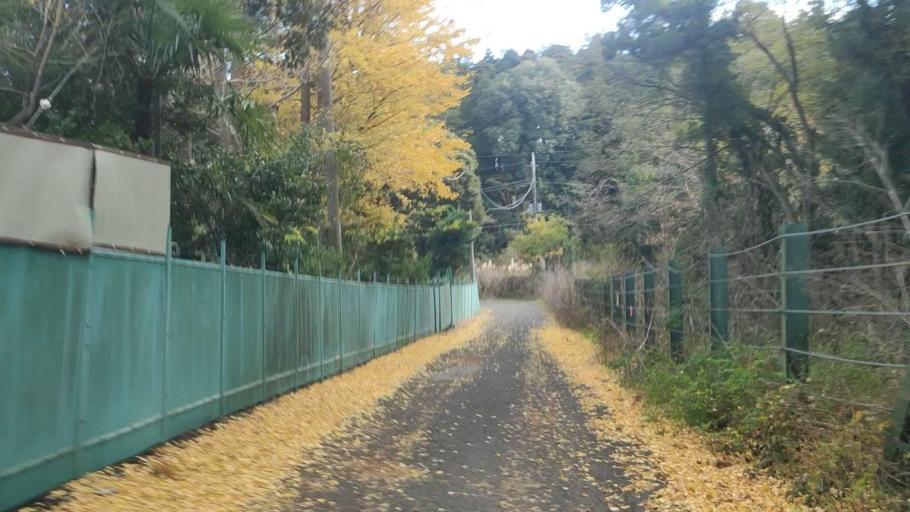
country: JP
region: Kanagawa
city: Minami-rinkan
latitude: 35.4815
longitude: 139.5022
